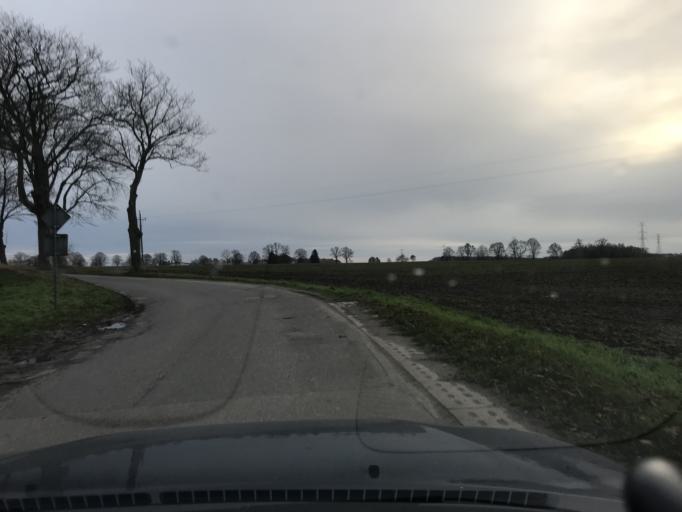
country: PL
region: Pomeranian Voivodeship
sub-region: Powiat slupski
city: Kobylnica
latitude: 54.4529
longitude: 16.8795
